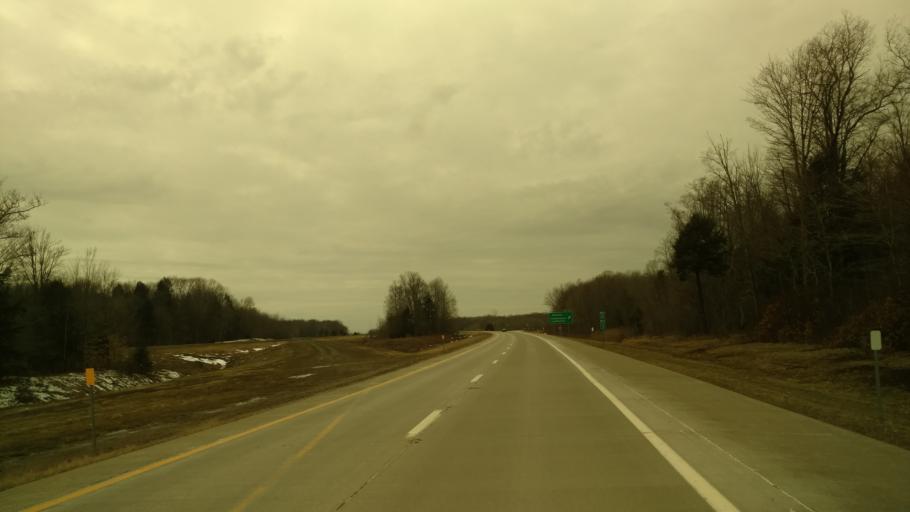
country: US
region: New York
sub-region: Chautauqua County
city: Mayville
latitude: 42.1570
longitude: -79.4650
